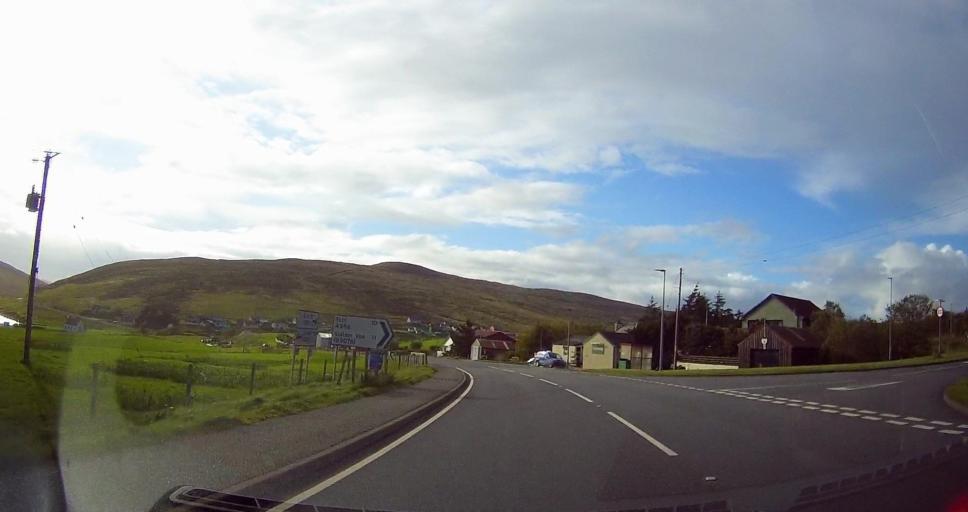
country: GB
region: Scotland
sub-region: Shetland Islands
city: Lerwick
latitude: 60.3547
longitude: -1.2617
